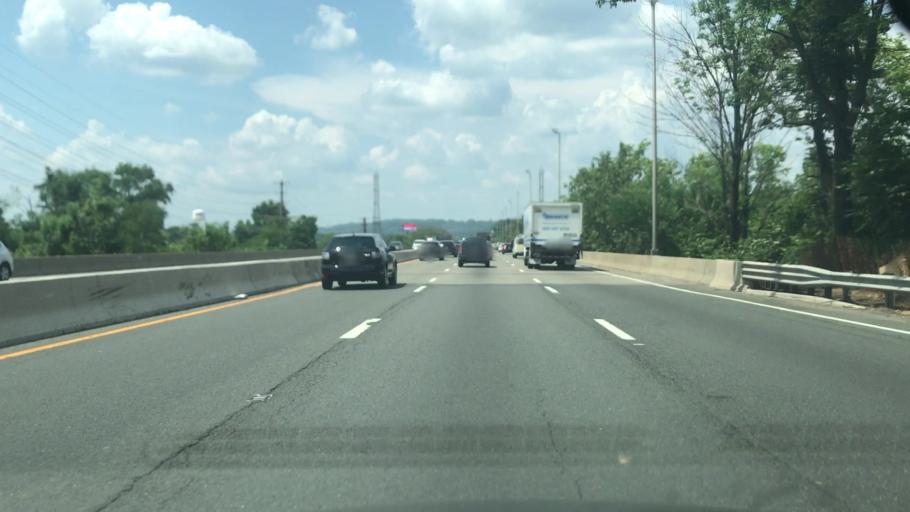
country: US
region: New Jersey
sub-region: Somerset County
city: South Bound Brook
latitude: 40.5531
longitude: -74.5434
